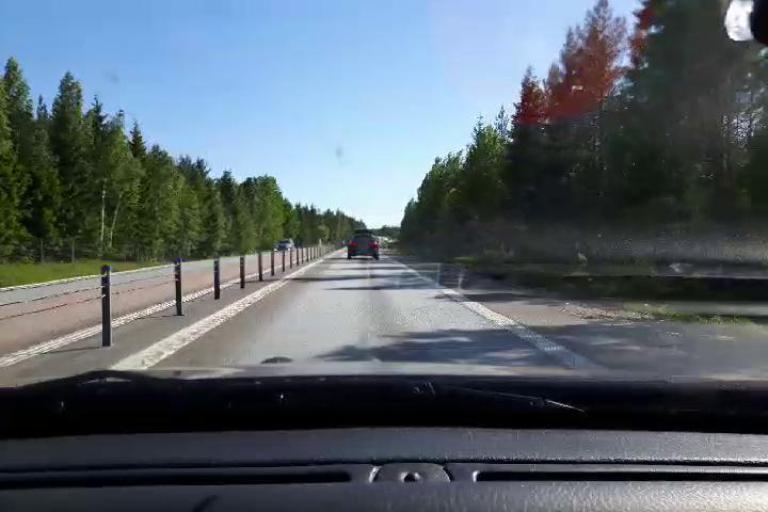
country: SE
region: Gaevleborg
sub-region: Gavle Kommun
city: Norrsundet
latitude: 60.8178
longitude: 17.0847
